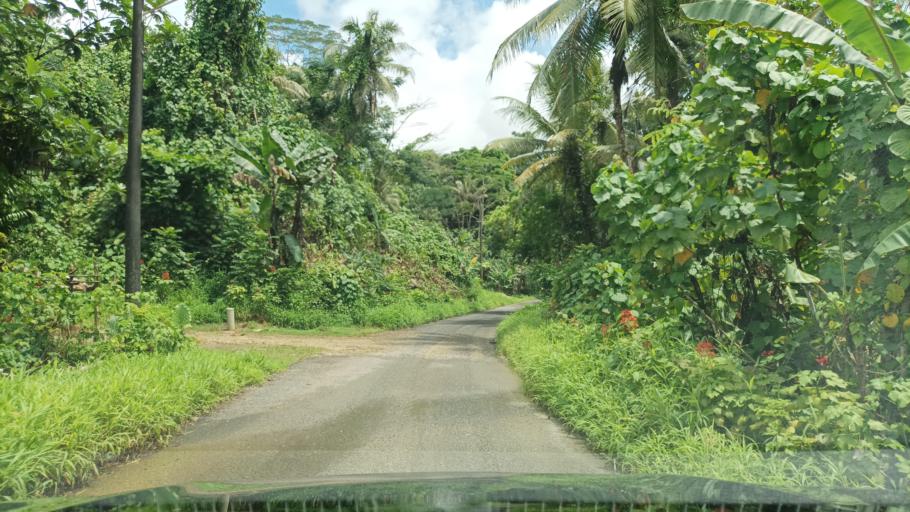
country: FM
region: Pohnpei
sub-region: Kolonia Municipality
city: Kolonia
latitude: 6.9643
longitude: 158.2244
